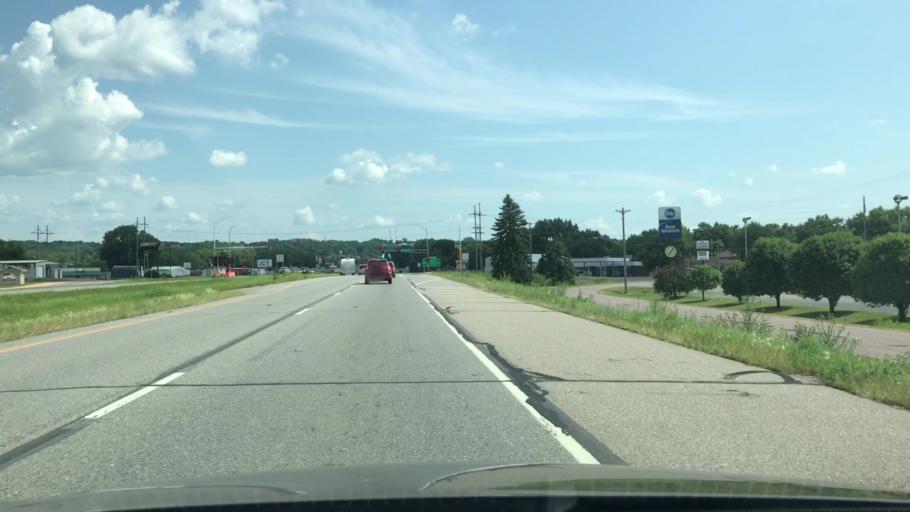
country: US
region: Minnesota
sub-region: Blue Earth County
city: Mankato
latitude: 44.1828
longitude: -94.0093
